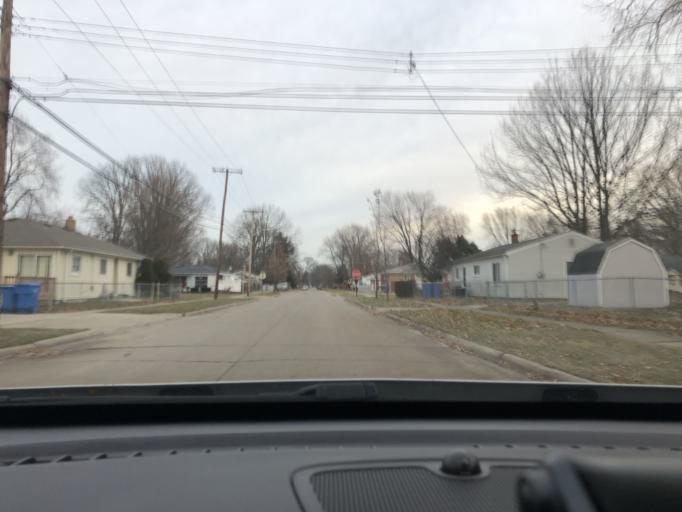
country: US
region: Michigan
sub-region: Wayne County
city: Allen Park
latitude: 42.2788
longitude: -83.2359
